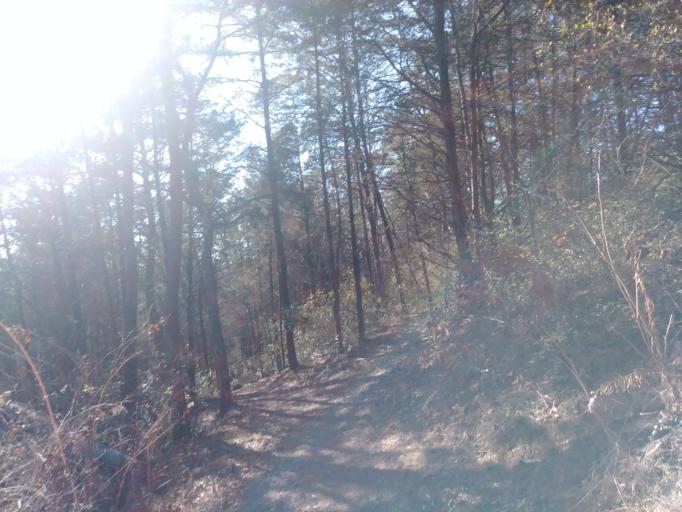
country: US
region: Tennessee
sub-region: Greene County
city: Greeneville
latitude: 36.1533
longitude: -82.8410
